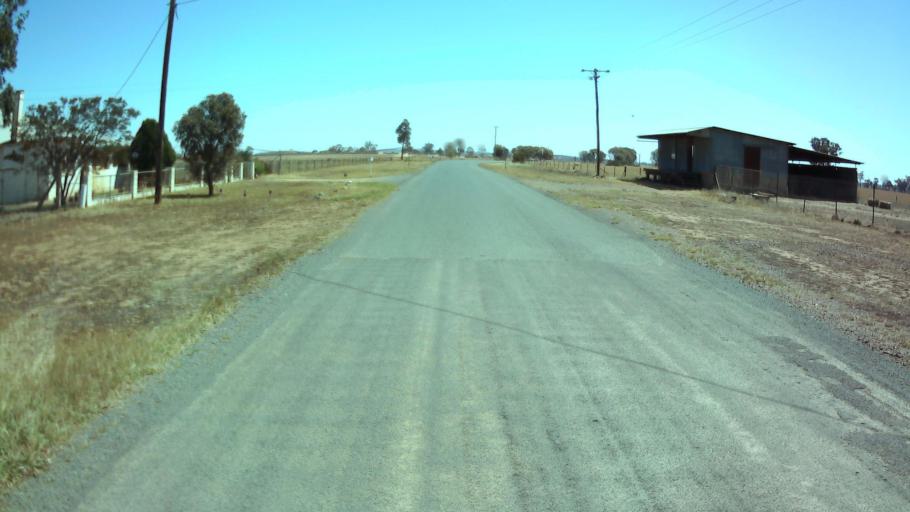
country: AU
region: New South Wales
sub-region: Weddin
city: Grenfell
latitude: -33.8409
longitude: 147.7444
